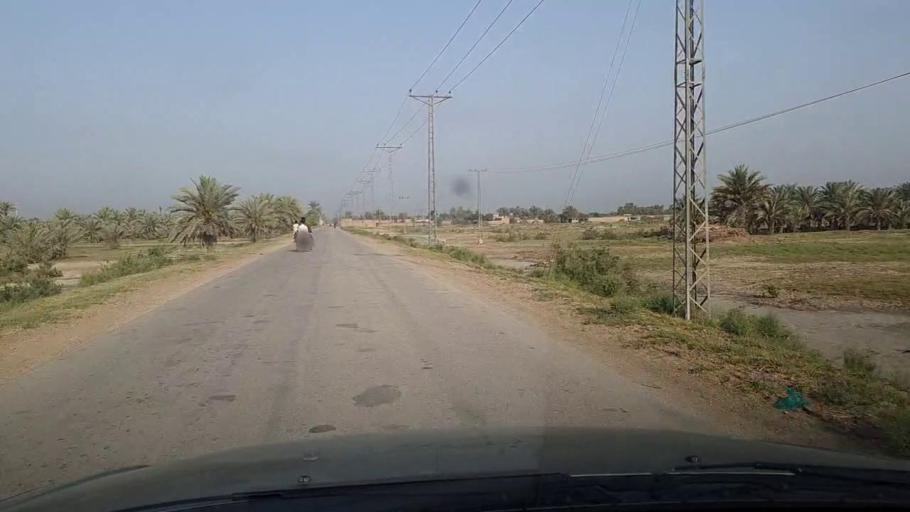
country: PK
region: Sindh
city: Pir jo Goth
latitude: 27.5695
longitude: 68.6329
